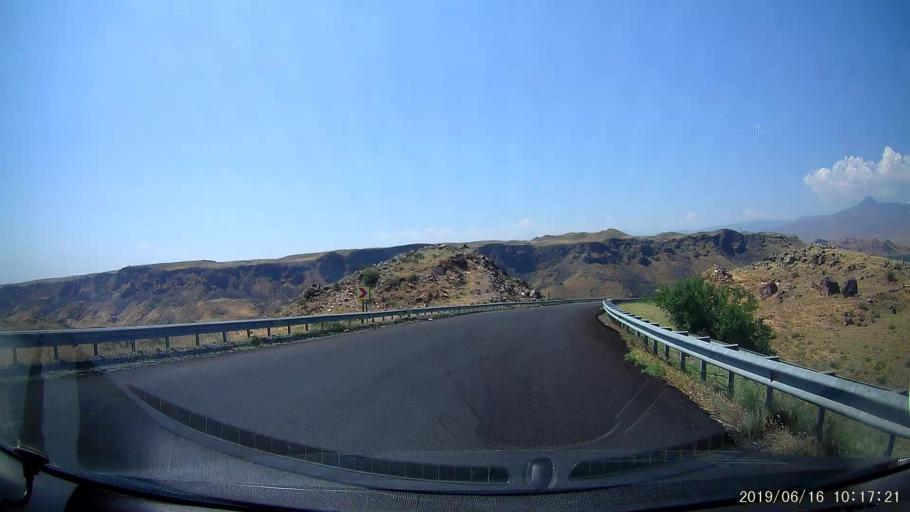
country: TR
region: Igdir
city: Tuzluca
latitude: 40.1686
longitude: 43.6822
